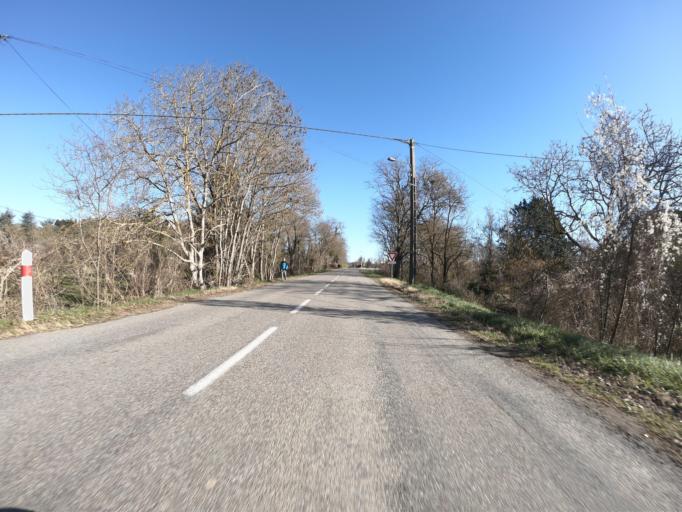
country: FR
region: Midi-Pyrenees
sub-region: Departement de l'Ariege
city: Mirepoix
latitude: 43.0965
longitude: 1.8748
